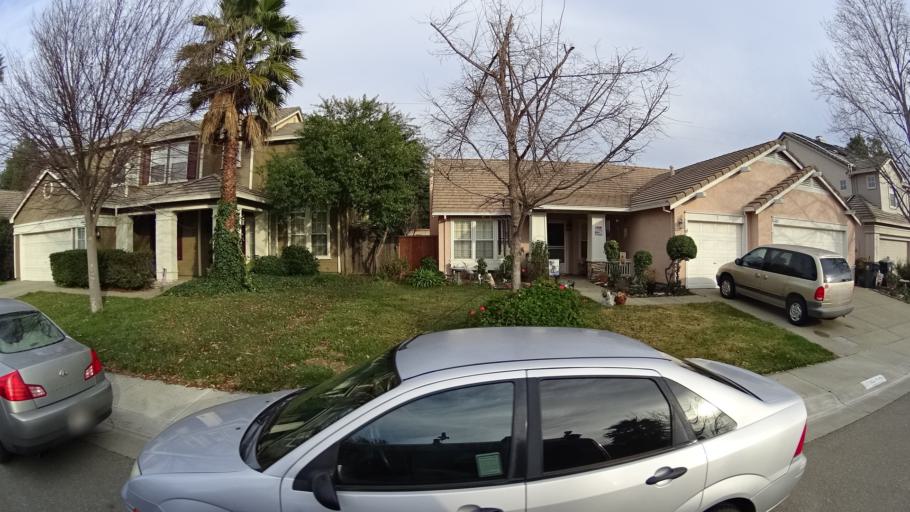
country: US
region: California
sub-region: Yolo County
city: Davis
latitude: 38.5635
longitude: -121.7116
